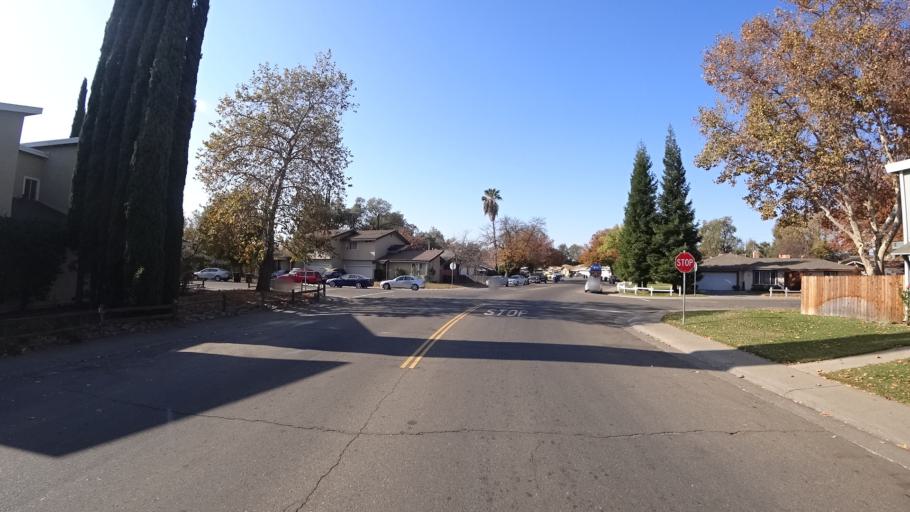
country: US
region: California
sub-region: Sacramento County
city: Citrus Heights
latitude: 38.6823
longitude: -121.2822
